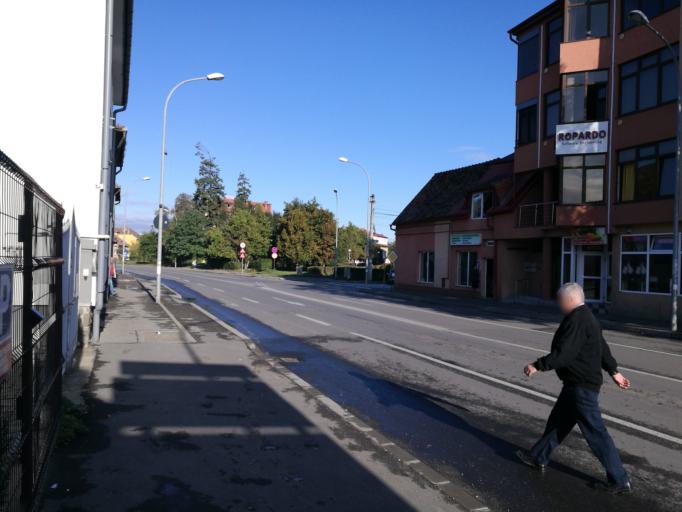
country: RO
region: Sibiu
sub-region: Municipiul Sibiu
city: Sibiu
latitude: 45.8000
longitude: 24.1432
